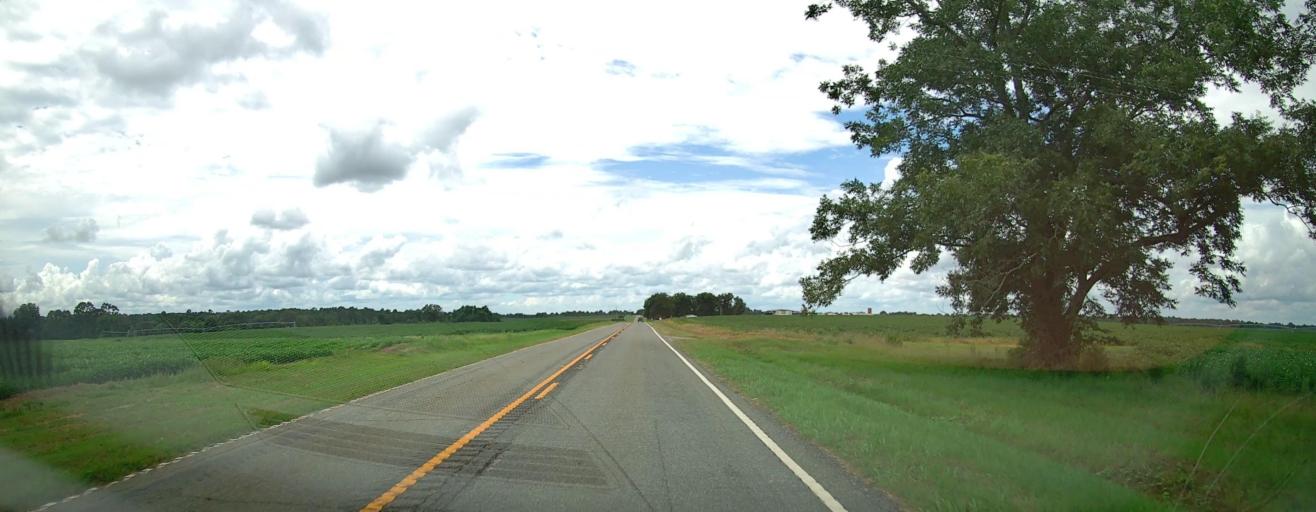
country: US
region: Georgia
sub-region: Dooly County
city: Unadilla
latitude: 32.2587
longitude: -83.7817
